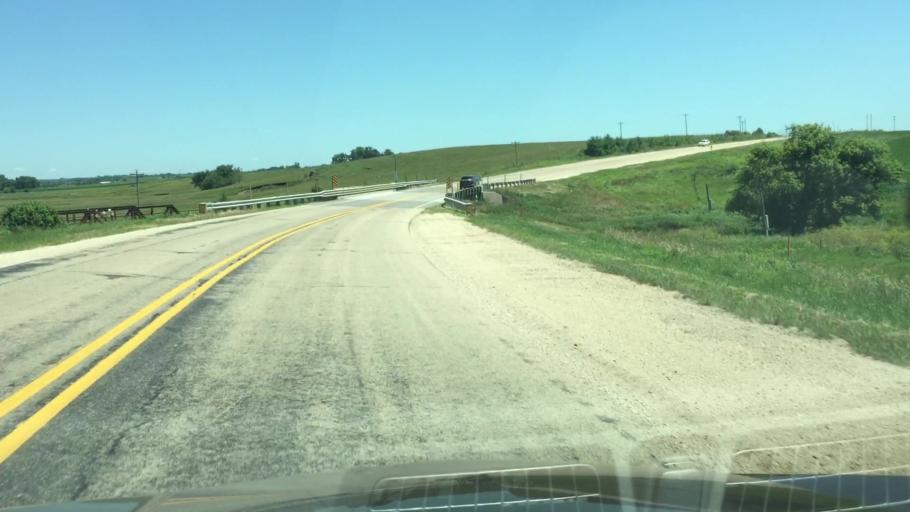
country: US
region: Iowa
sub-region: Cedar County
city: Mechanicsville
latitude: 41.9608
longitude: -91.1505
